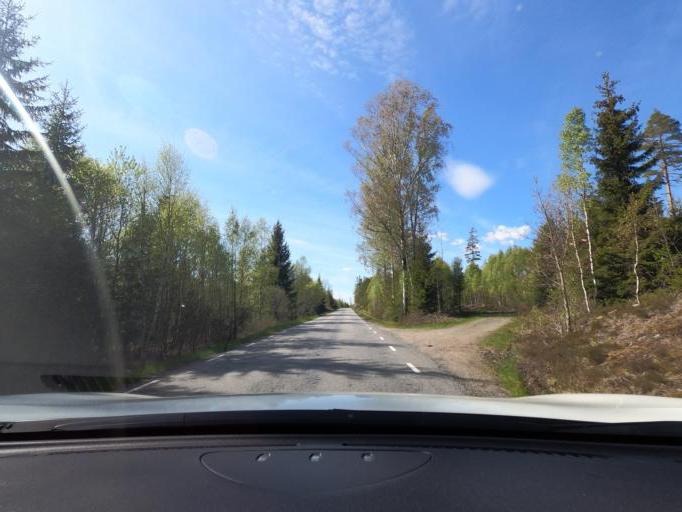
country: SE
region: Vaestra Goetaland
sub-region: Marks Kommun
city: Bua
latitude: 57.4904
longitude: 12.5600
